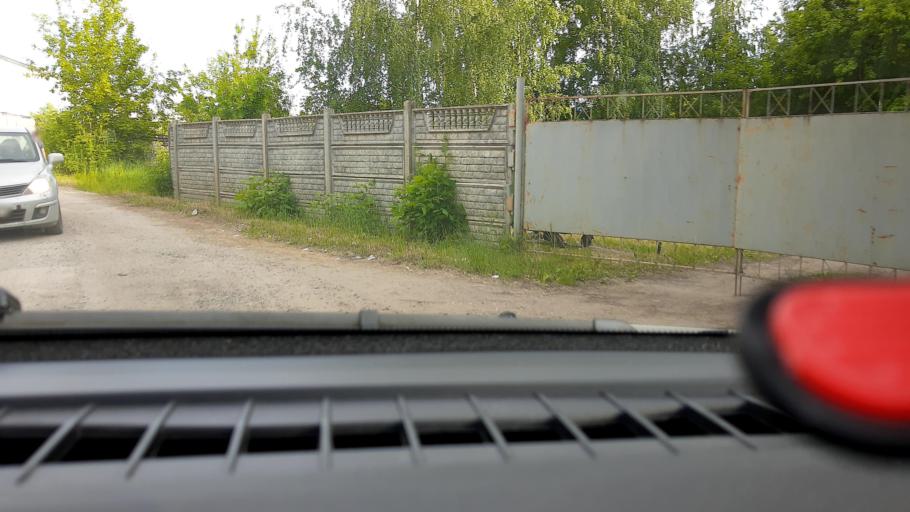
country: RU
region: Nizjnij Novgorod
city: Neklyudovo
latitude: 56.3490
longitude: 43.8814
